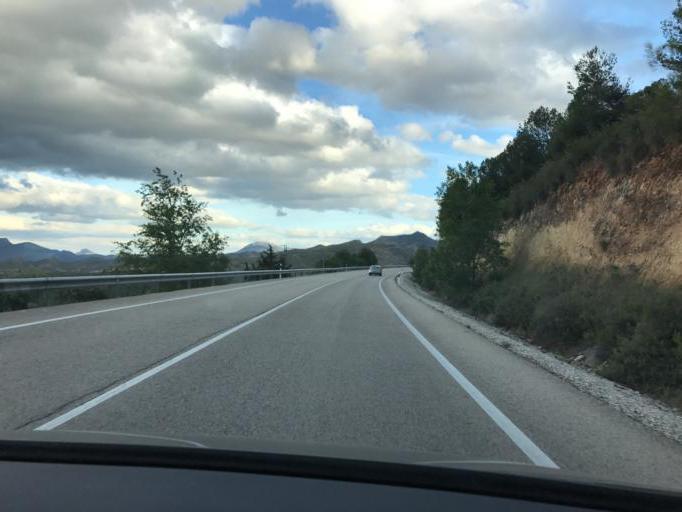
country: ES
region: Andalusia
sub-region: Provincia de Jaen
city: Jodar
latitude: 37.7910
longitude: -3.3367
